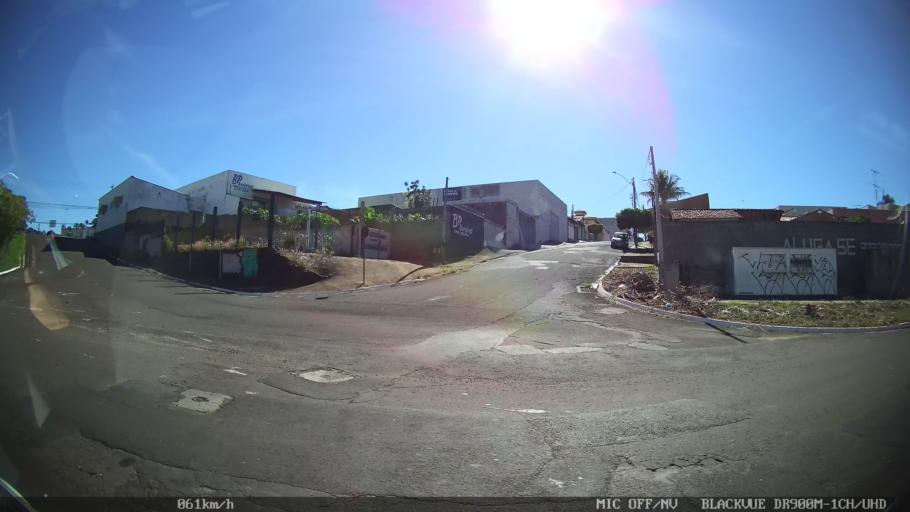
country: BR
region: Sao Paulo
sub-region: Franca
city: Franca
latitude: -20.5207
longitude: -47.3830
